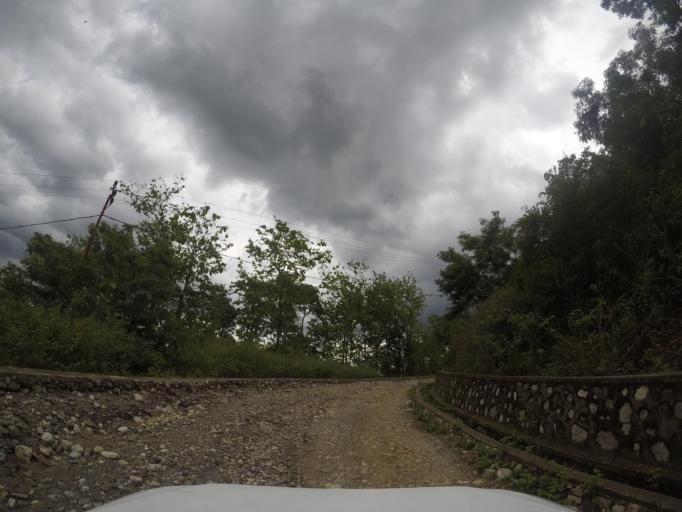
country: TL
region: Bobonaro
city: Maliana
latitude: -8.9730
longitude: 125.2297
